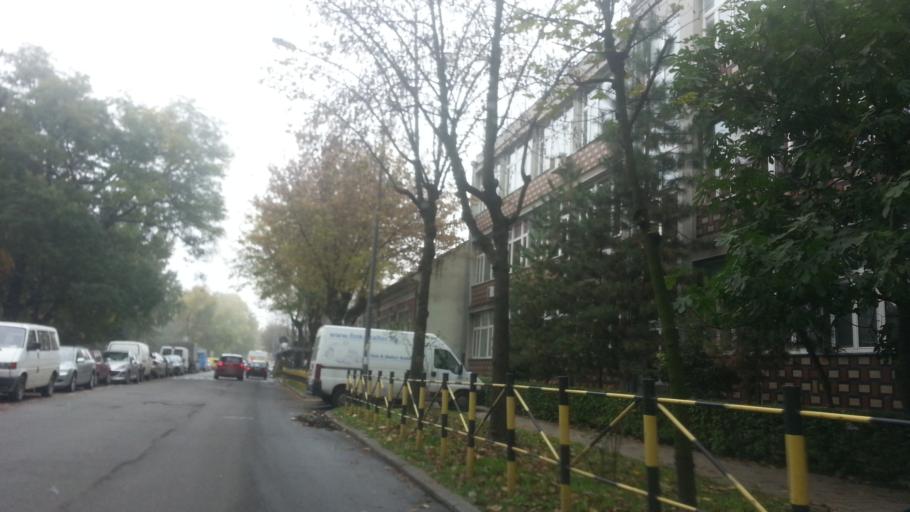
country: RS
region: Central Serbia
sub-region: Belgrade
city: Zemun
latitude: 44.8456
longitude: 20.4153
